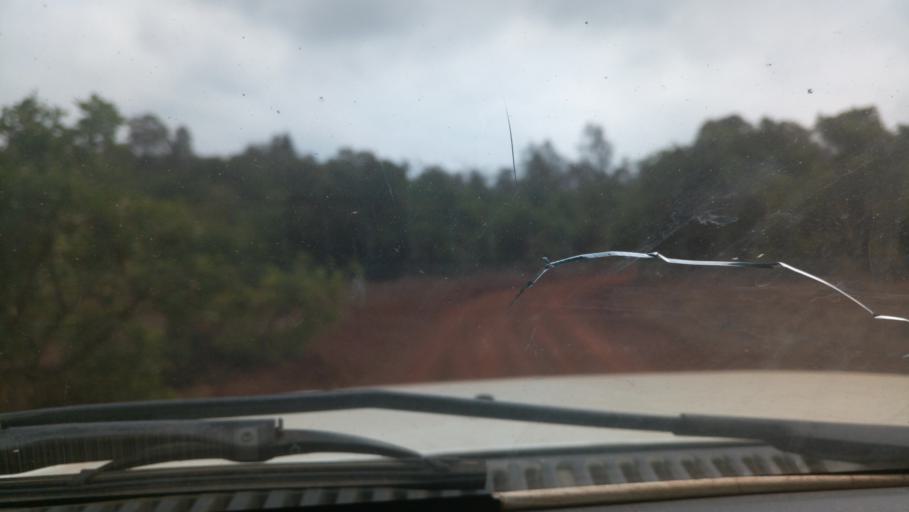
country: KE
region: Nairobi Area
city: Nairobi
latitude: -1.3578
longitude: 36.7777
